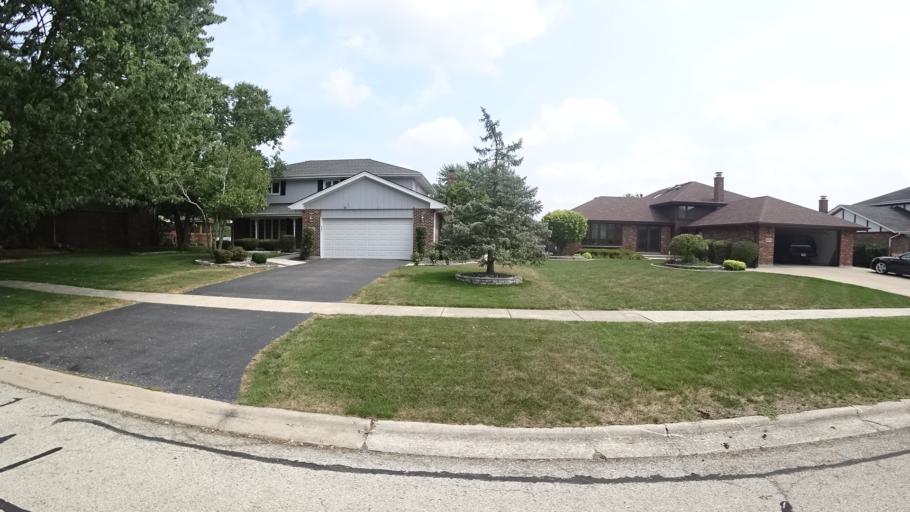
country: US
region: Illinois
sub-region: Will County
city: Goodings Grove
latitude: 41.6221
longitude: -87.9093
